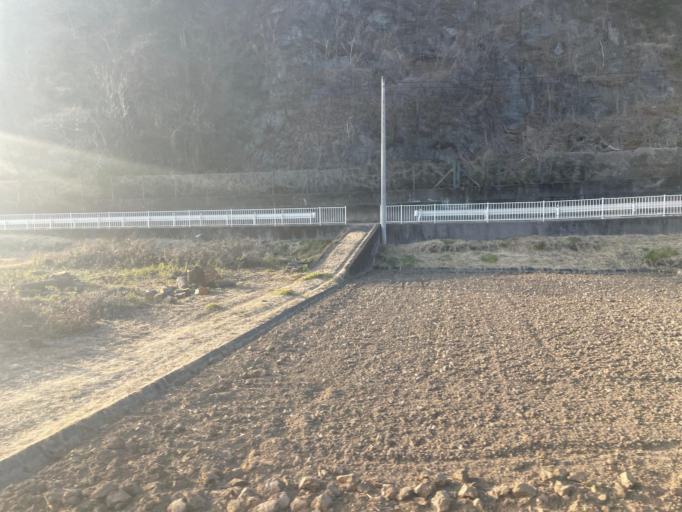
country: JP
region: Gunma
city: Shibukawa
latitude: 36.5497
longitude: 138.9411
